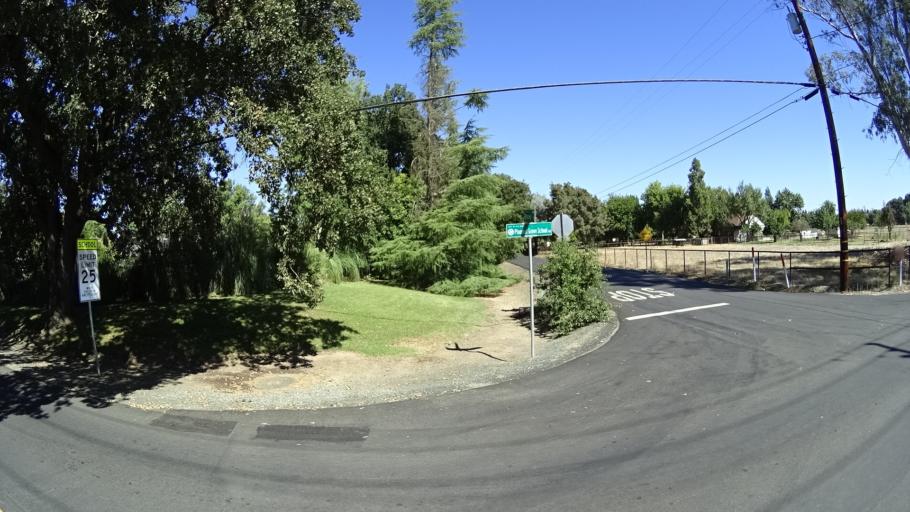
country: US
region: California
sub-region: Sacramento County
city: Wilton
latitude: 38.4308
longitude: -121.3113
